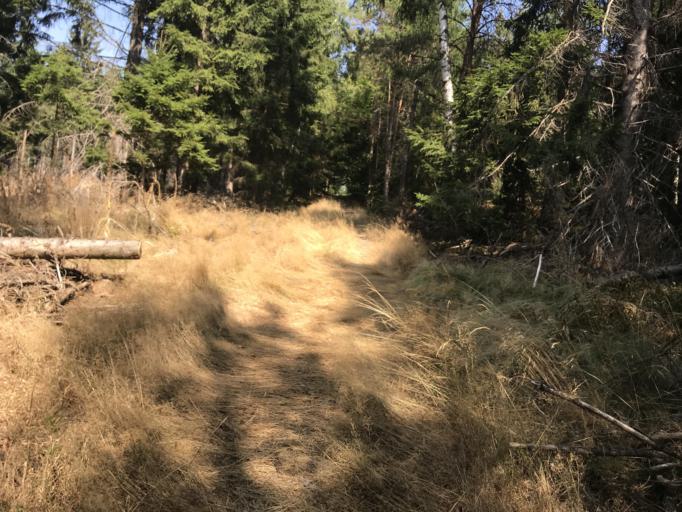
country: DE
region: Rheinland-Pfalz
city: Oestrich-Winkel
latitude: 50.0476
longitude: 8.0086
